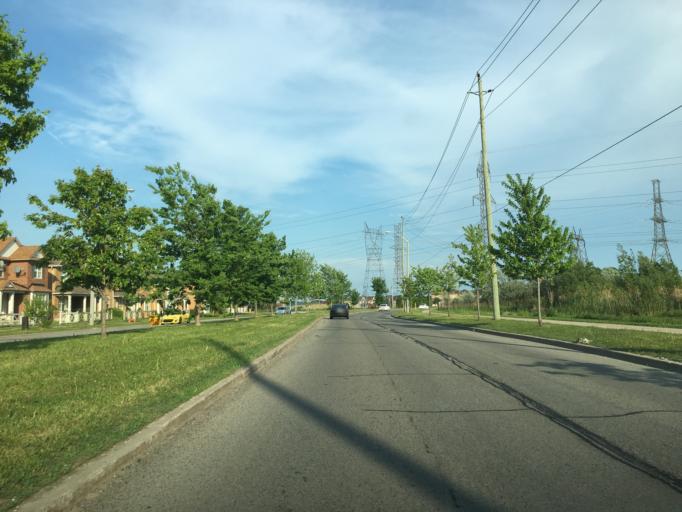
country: CA
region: Ontario
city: Markham
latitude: 43.8270
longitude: -79.2344
